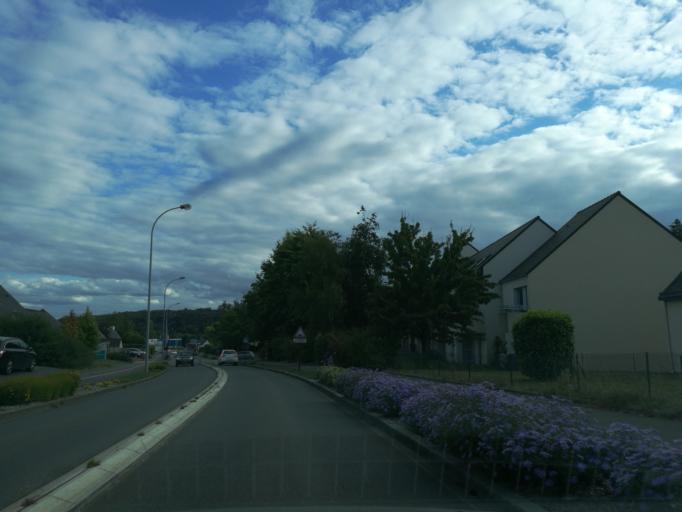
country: FR
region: Brittany
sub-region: Departement d'Ille-et-Vilaine
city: Montfort-sur-Meu
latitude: 48.1359
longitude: -1.9476
